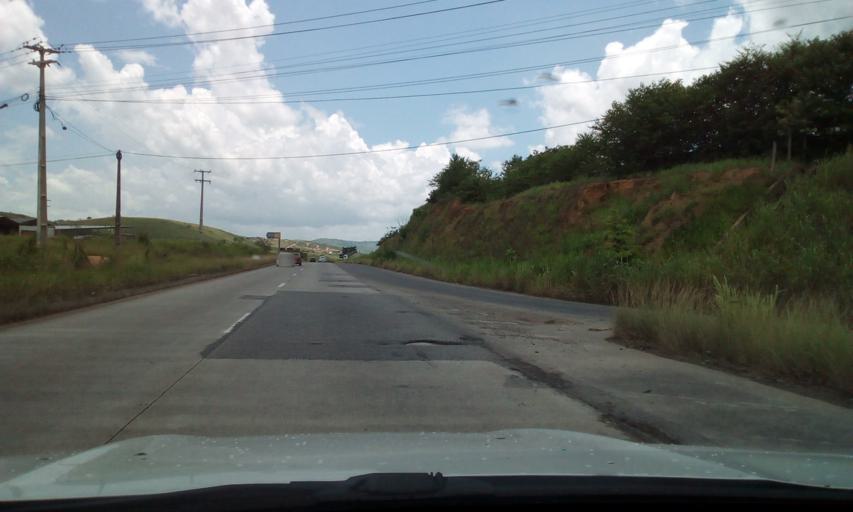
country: BR
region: Pernambuco
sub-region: Vitoria De Santo Antao
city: Vitoria de Santo Antao
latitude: -8.1187
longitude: -35.2634
